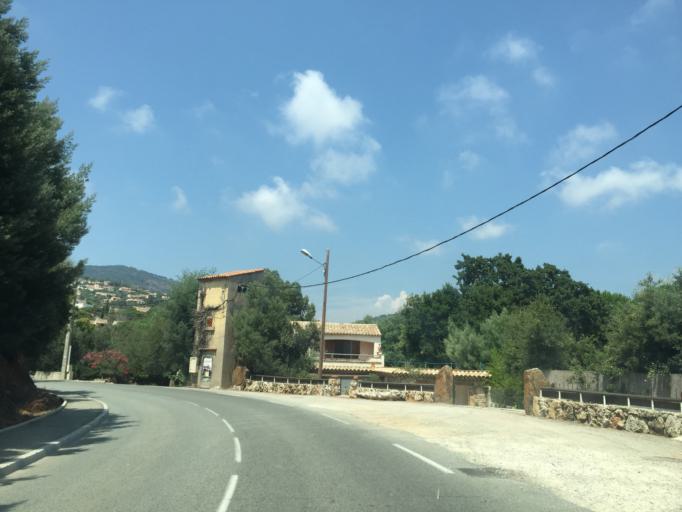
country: FR
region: Provence-Alpes-Cote d'Azur
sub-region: Departement du Var
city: Sainte-Maxime
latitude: 43.3429
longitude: 6.6793
